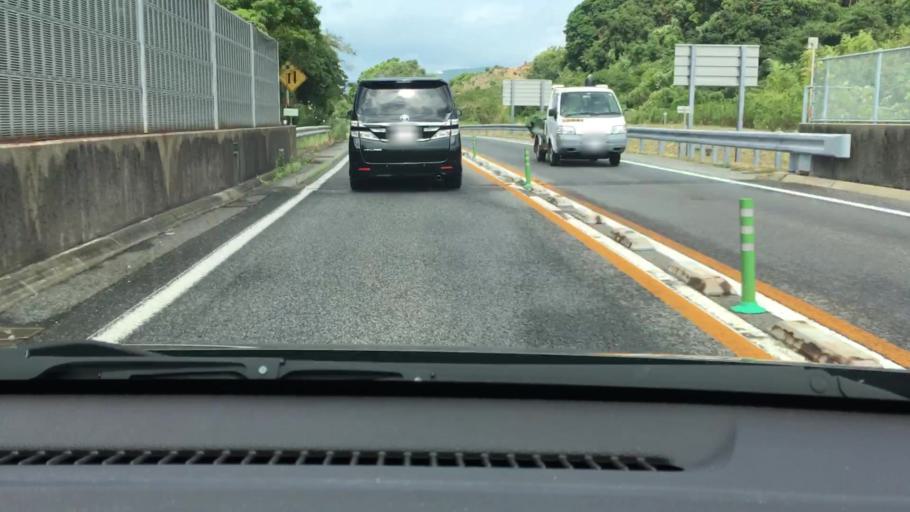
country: JP
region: Nagasaki
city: Sasebo
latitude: 33.1511
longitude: 129.7650
